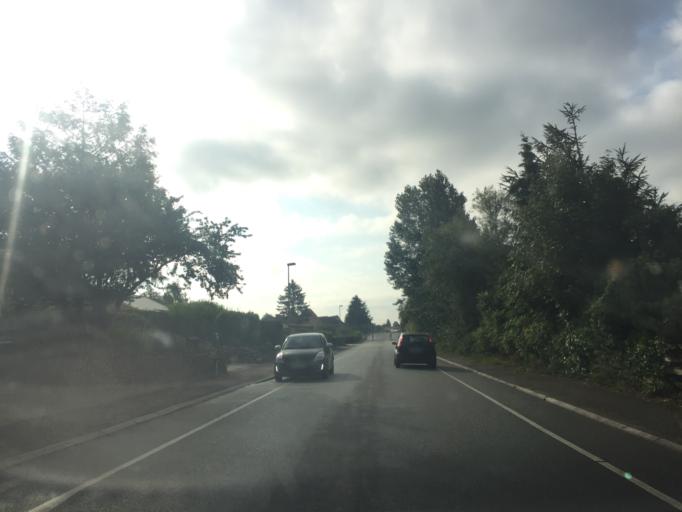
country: DK
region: Capital Region
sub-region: Halsnaes Kommune
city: Frederiksvaerk
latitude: 55.9514
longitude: 12.0299
